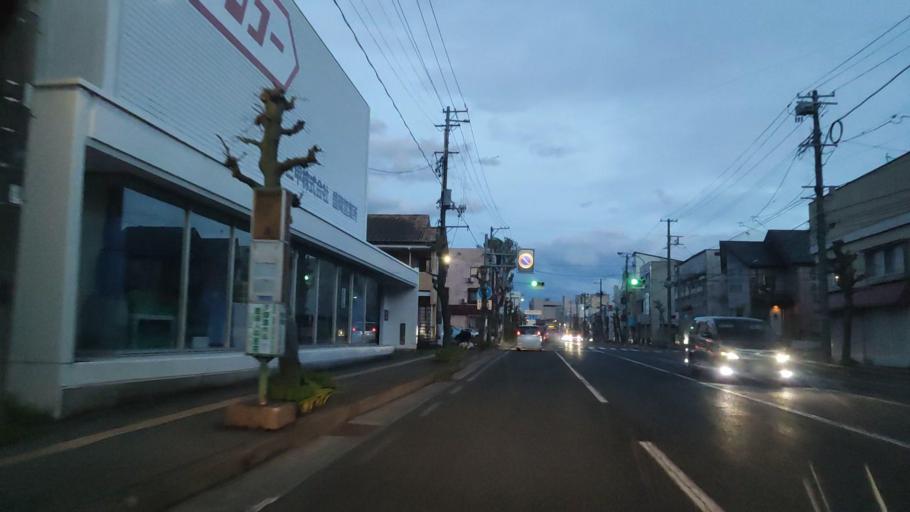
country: JP
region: Iwate
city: Morioka-shi
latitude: 39.7105
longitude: 141.1324
